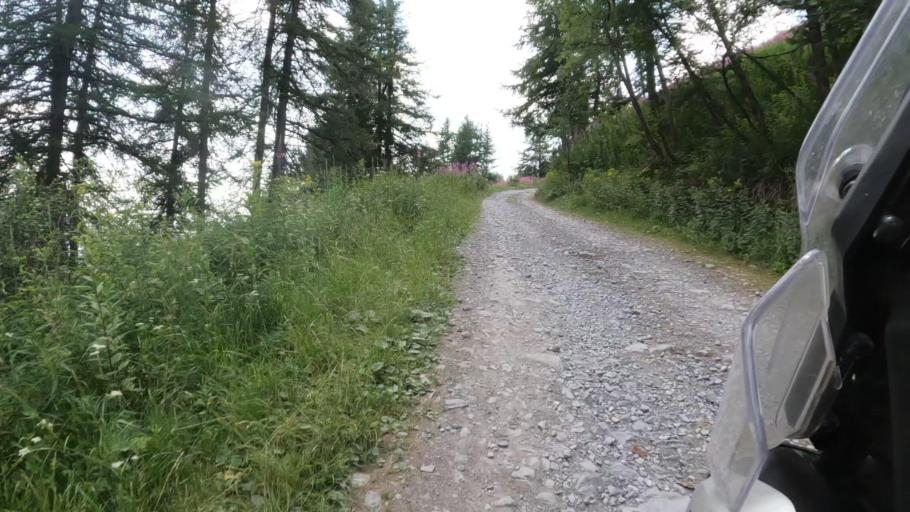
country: FR
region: Provence-Alpes-Cote d'Azur
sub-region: Departement des Alpes-Maritimes
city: Tende
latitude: 44.0257
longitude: 7.6638
